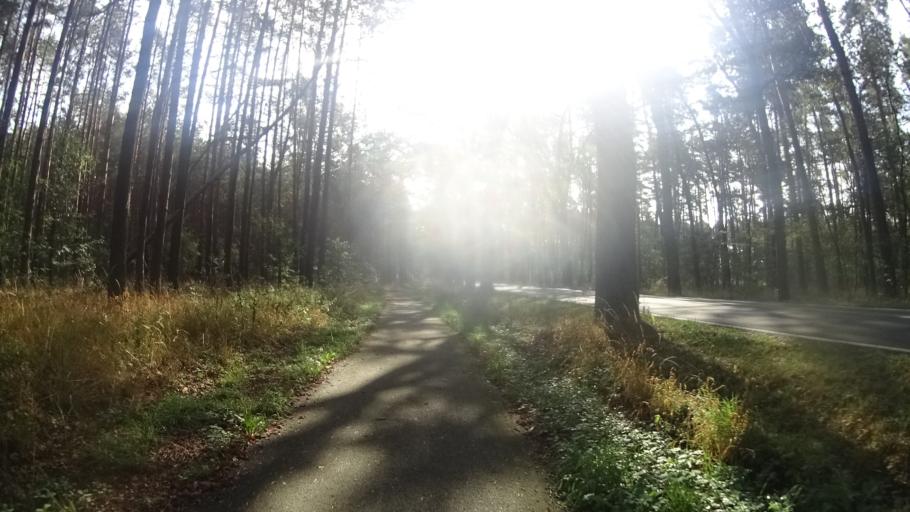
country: DE
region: Brandenburg
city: Cumlosen
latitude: 53.0218
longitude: 11.6885
